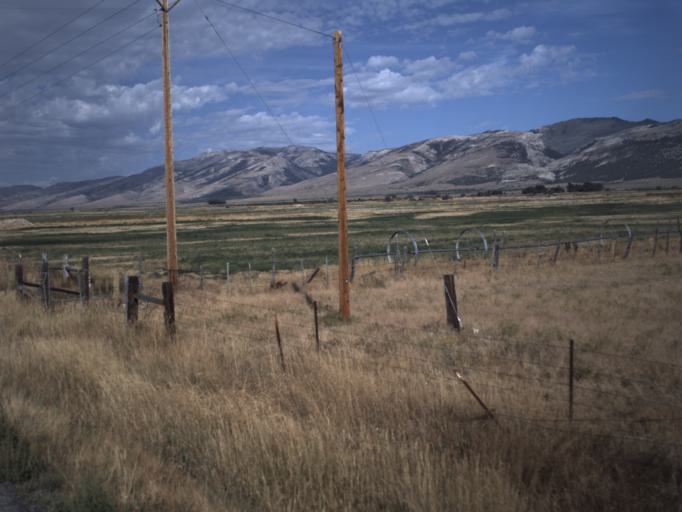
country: US
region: Idaho
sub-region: Cassia County
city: Burley
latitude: 41.8170
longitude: -113.3350
